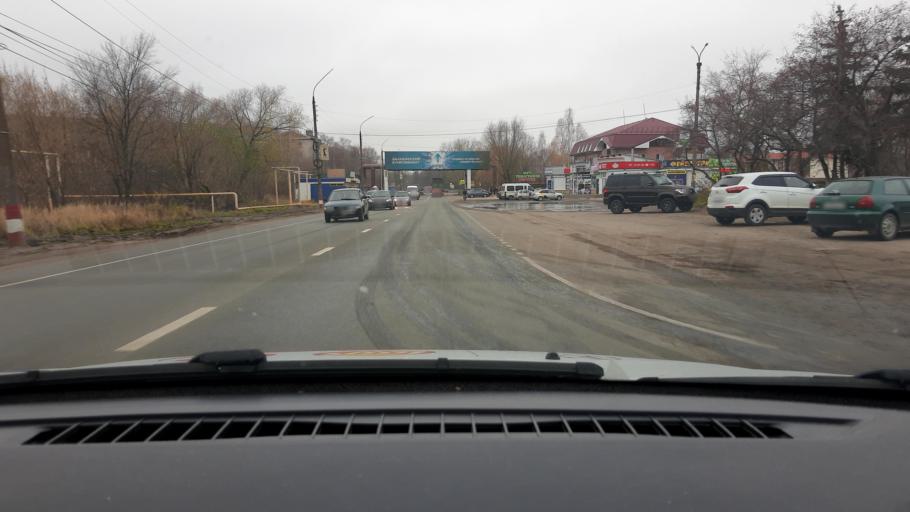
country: RU
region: Nizjnij Novgorod
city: Novaya Balakhna
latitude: 56.5204
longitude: 43.5727
